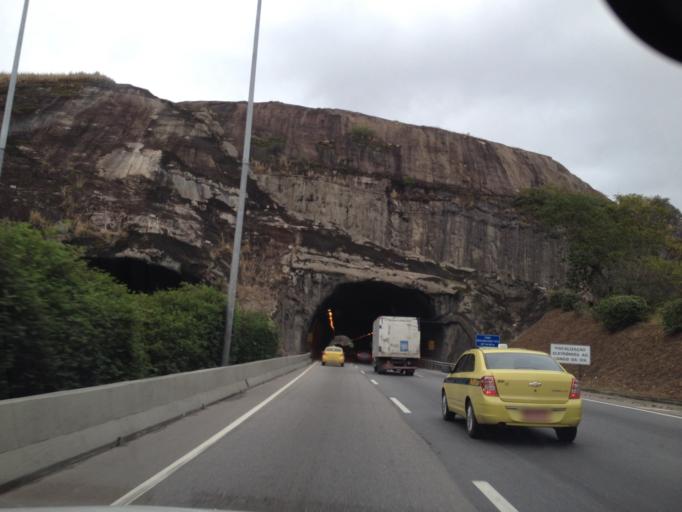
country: BR
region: Rio de Janeiro
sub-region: Sao Joao De Meriti
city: Sao Joao de Meriti
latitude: -22.9286
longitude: -43.3430
